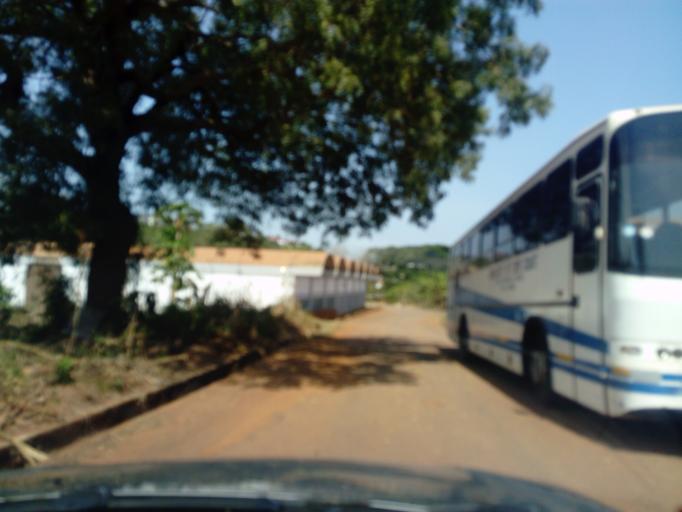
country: GH
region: Central
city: Cape Coast
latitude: 5.1077
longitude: -1.2808
